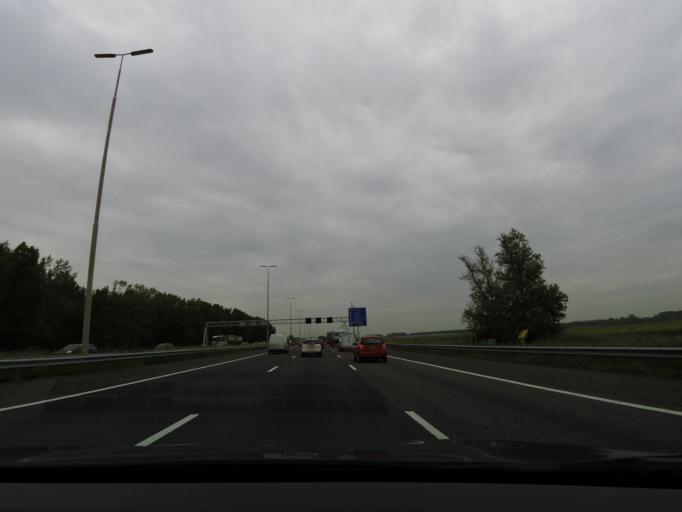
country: NL
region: South Holland
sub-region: Gemeente Voorschoten
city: Voorschoten
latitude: 52.1184
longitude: 4.4713
